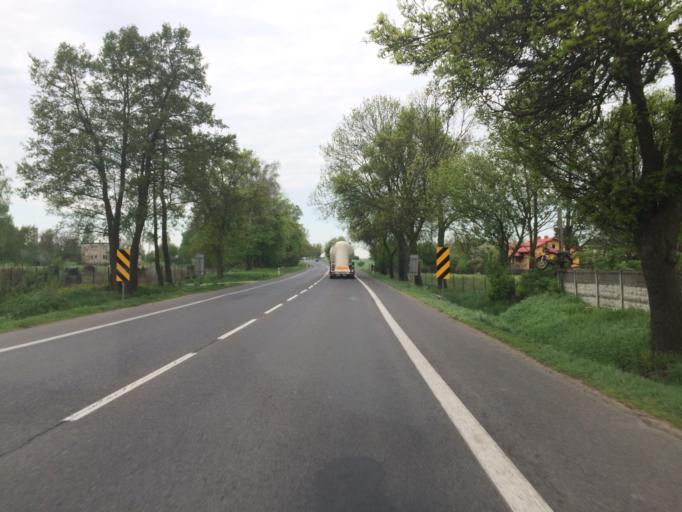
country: PL
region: Masovian Voivodeship
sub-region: Powiat mlawski
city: Wisniewo
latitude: 53.0844
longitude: 20.3591
